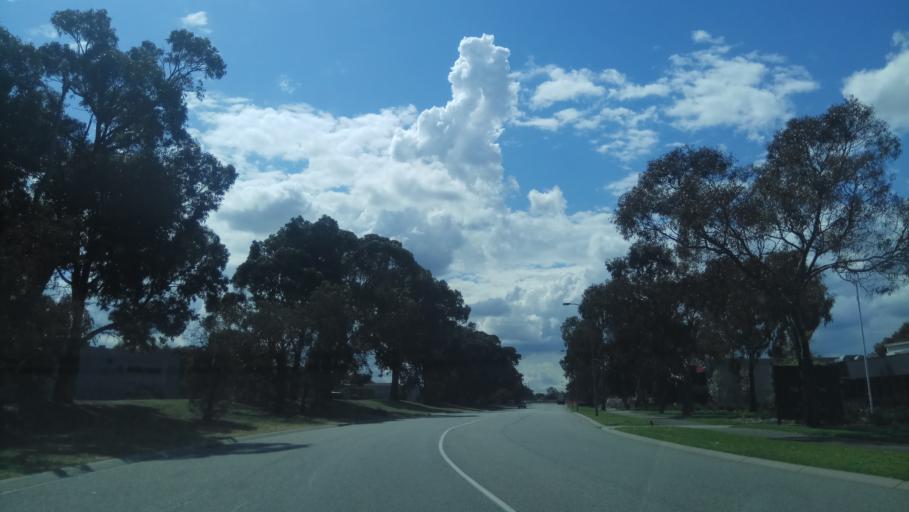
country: AU
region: Victoria
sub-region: Kingston
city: Dingley Village
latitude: -37.9910
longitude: 145.1172
